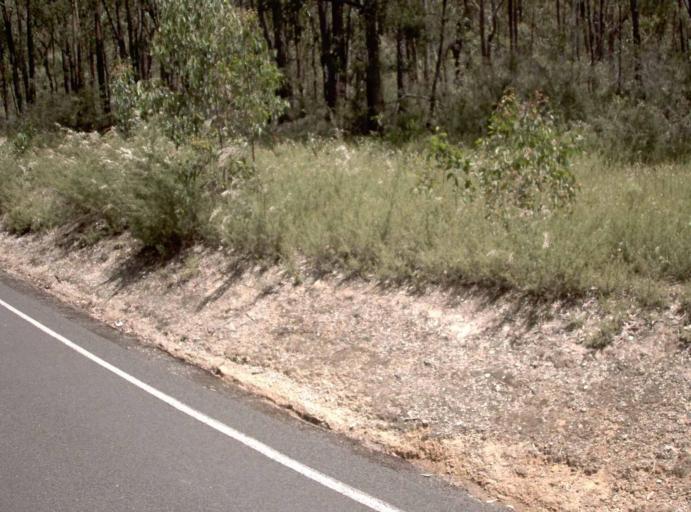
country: AU
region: Victoria
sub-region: East Gippsland
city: Lakes Entrance
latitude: -37.5943
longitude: 147.8926
